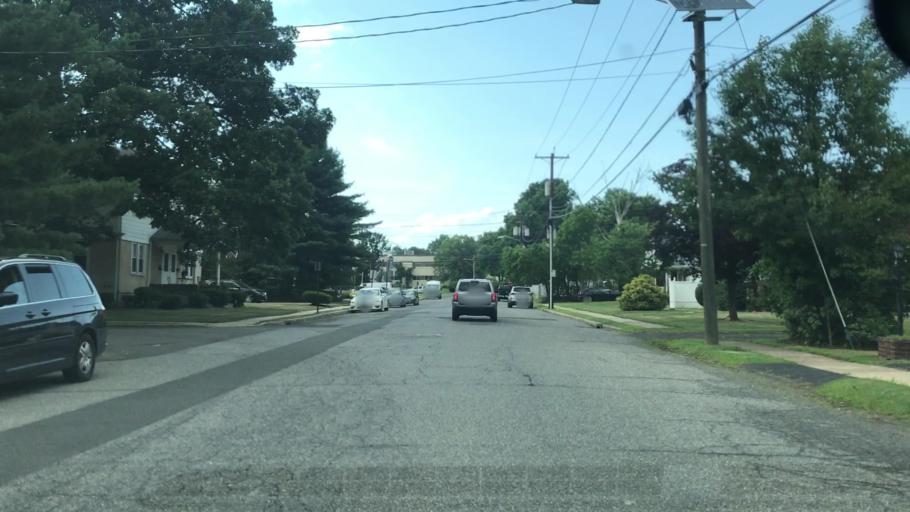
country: US
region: New Jersey
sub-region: Somerset County
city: Raritan
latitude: 40.5729
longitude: -74.6370
